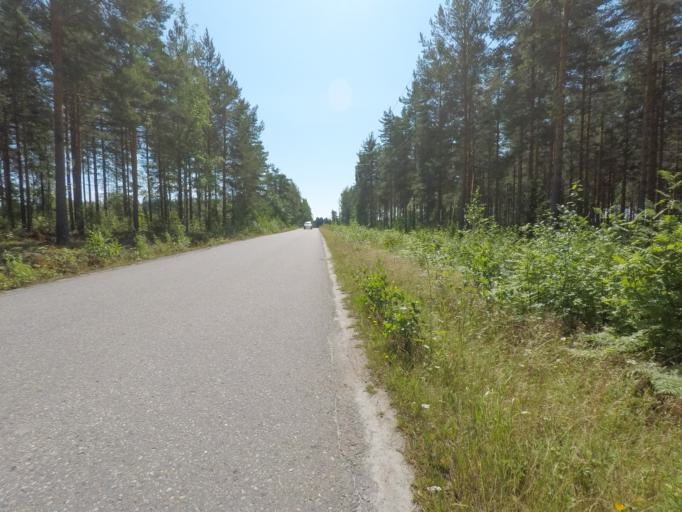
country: FI
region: Southern Savonia
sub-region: Mikkeli
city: Puumala
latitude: 61.4495
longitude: 28.1585
